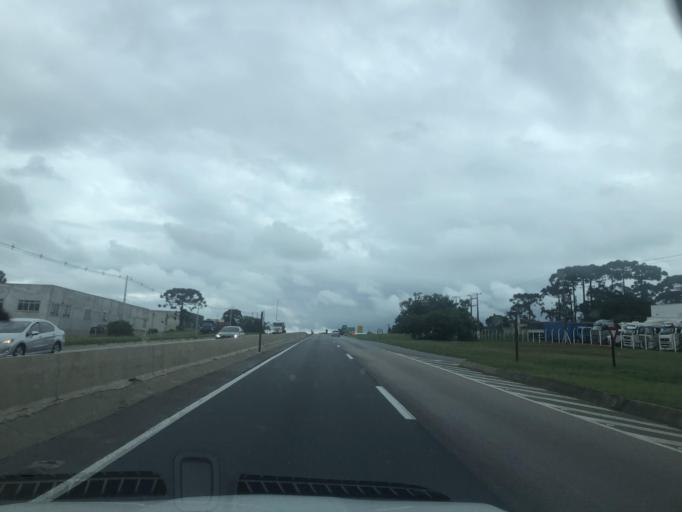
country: BR
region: Parana
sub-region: Araucaria
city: Araucaria
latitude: -25.6842
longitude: -49.3164
